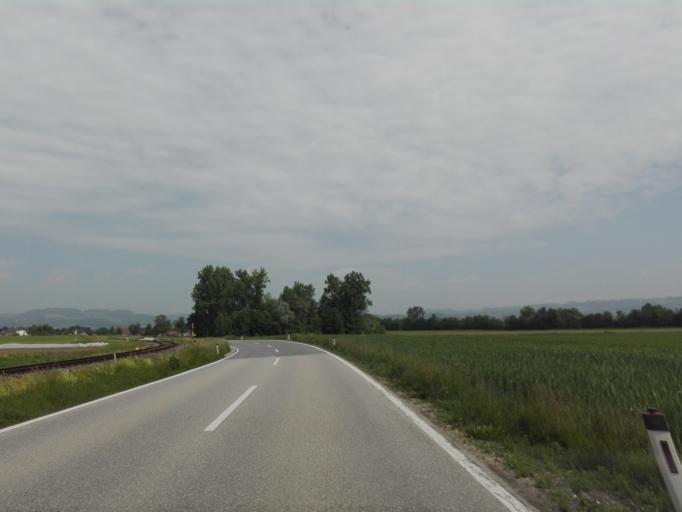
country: AT
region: Upper Austria
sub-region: Politischer Bezirk Urfahr-Umgebung
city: Feldkirchen an der Donau
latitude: 48.3435
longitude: 13.9984
